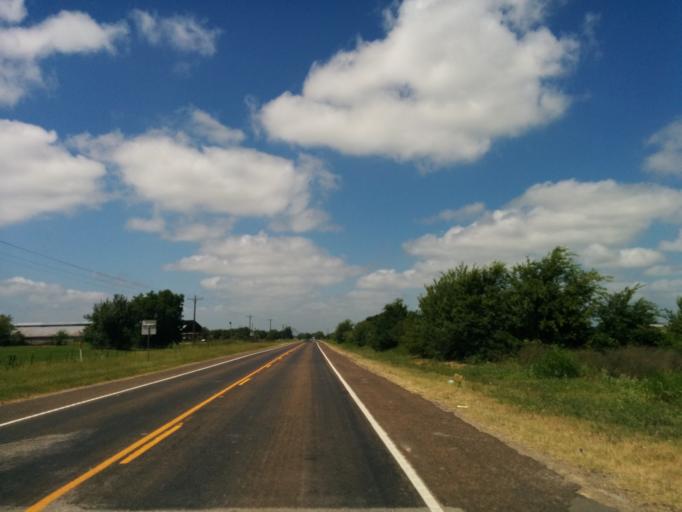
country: US
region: Texas
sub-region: Houston County
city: Crockett
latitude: 31.2943
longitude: -95.4996
